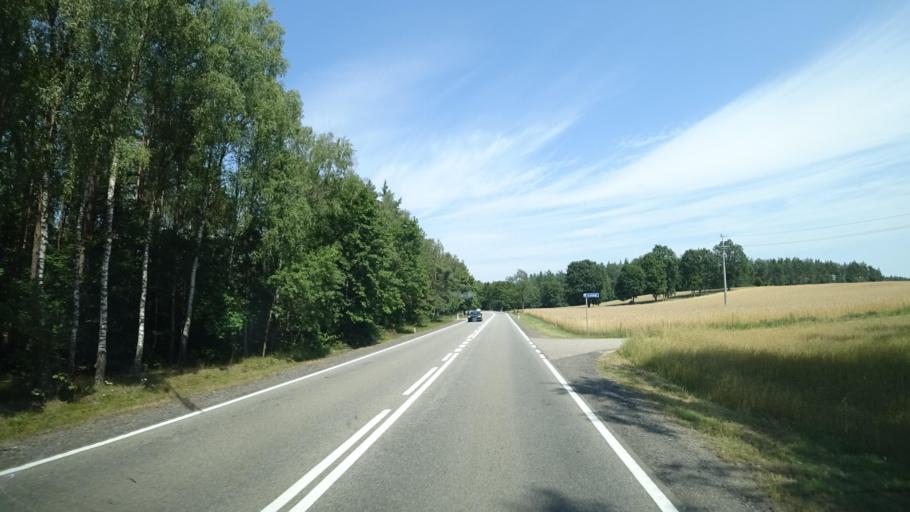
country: PL
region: Pomeranian Voivodeship
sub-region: Powiat koscierski
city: Grabowo Koscierskie
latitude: 54.1934
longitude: 18.1119
